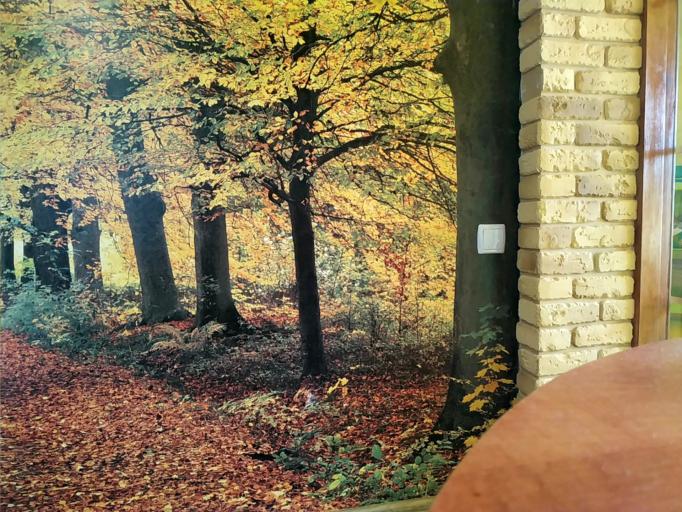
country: RU
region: Novgorod
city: Sol'tsy
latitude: 57.9042
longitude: 30.2229
